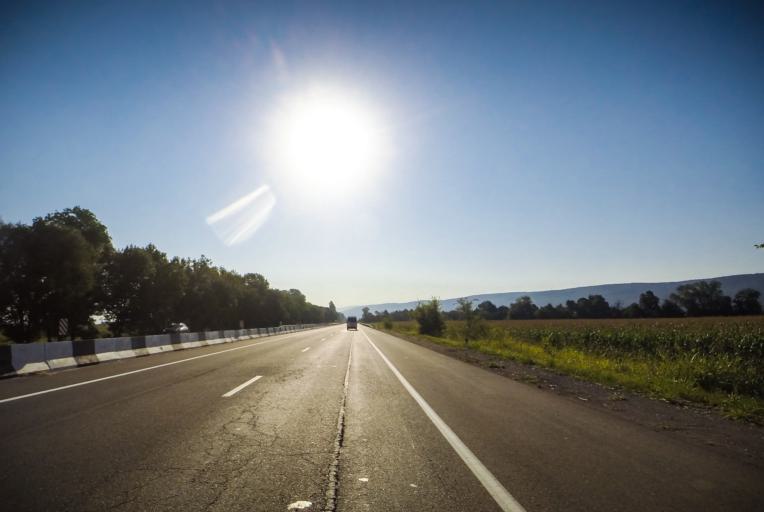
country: RU
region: North Ossetia
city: Zmeyskaya
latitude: 43.3229
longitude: 44.1188
